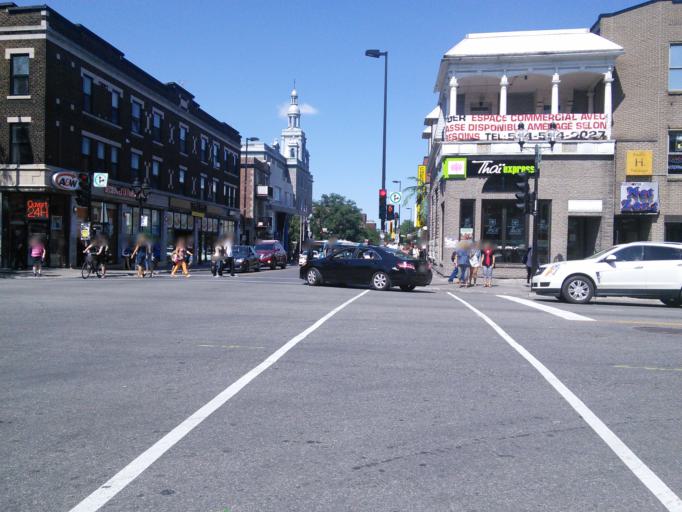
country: CA
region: Quebec
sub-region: Montreal
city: Montreal
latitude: 45.5239
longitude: -73.5830
